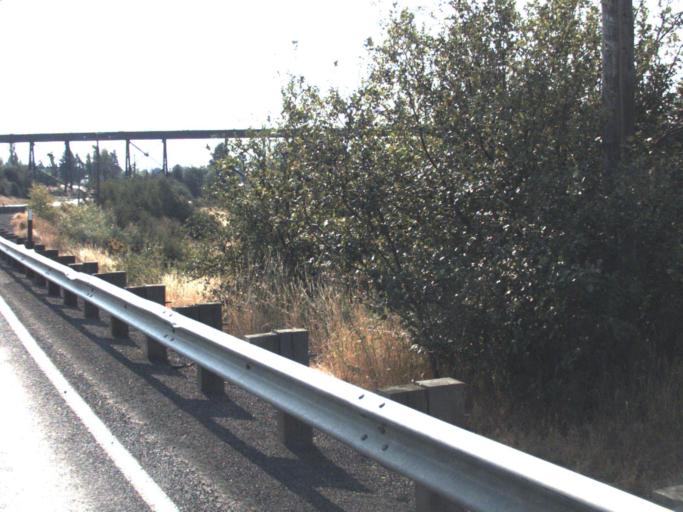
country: US
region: Idaho
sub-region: Benewah County
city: Plummer
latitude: 47.2289
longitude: -117.0820
